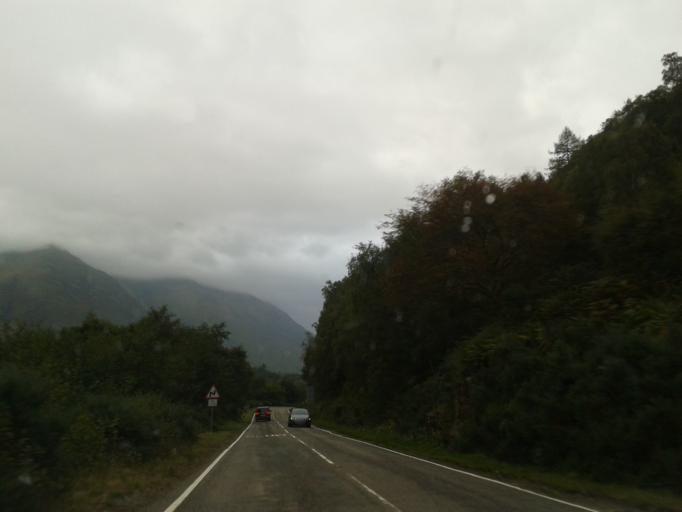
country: GB
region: Scotland
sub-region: Highland
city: Fort William
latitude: 57.2115
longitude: -5.4119
